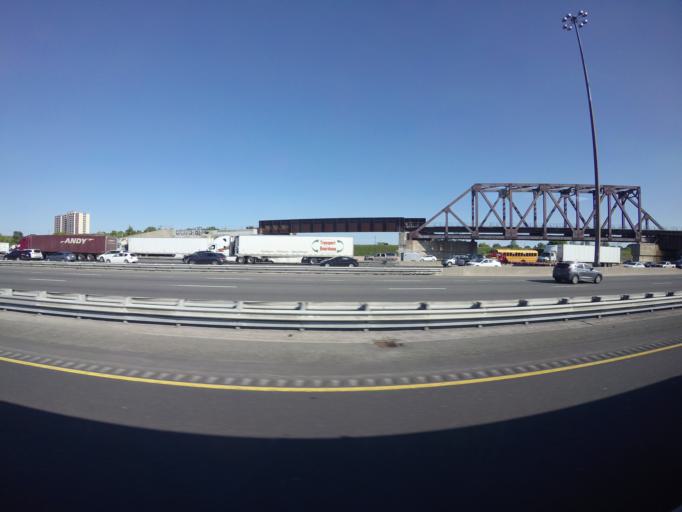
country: CA
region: Ontario
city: Ajax
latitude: 43.8270
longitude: -79.0973
